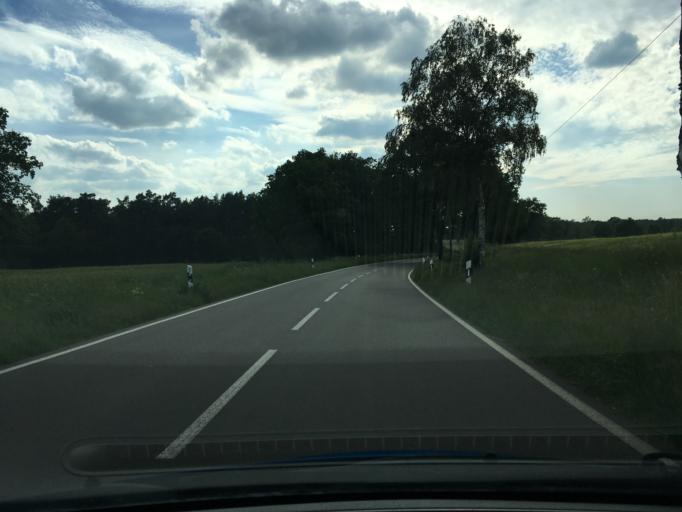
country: DE
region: Lower Saxony
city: Wistedt
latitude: 53.2716
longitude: 9.6644
